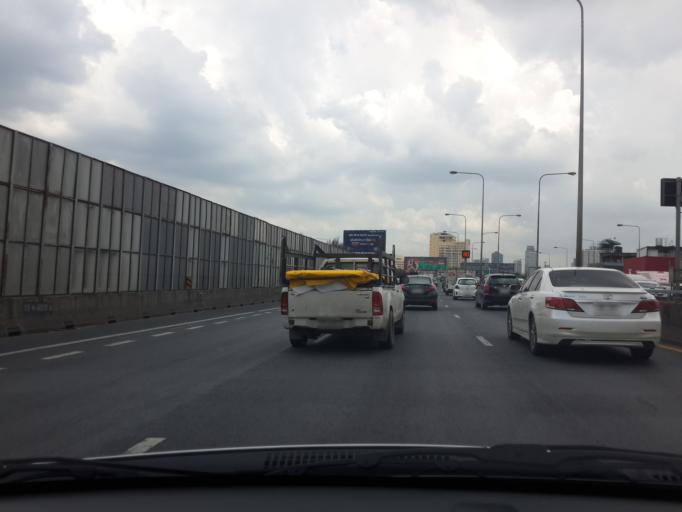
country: TH
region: Bangkok
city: Khlong Toei
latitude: 13.7125
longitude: 100.5698
